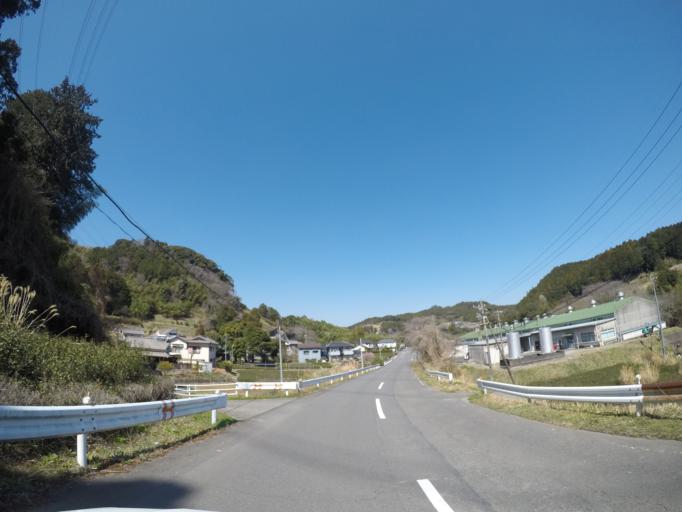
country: JP
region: Shizuoka
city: Kanaya
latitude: 34.7894
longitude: 138.1255
